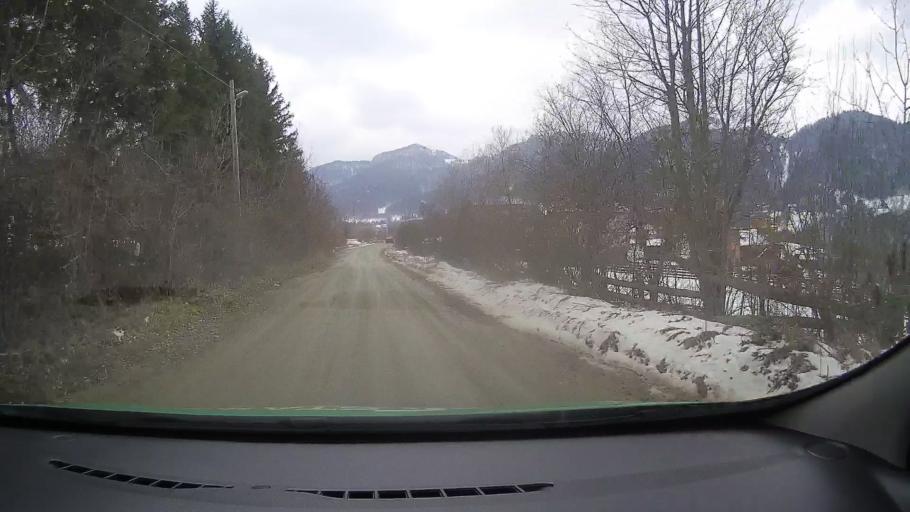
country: RO
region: Brasov
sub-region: Comuna Zarnesti
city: Zarnesti
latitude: 45.5472
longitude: 25.3222
